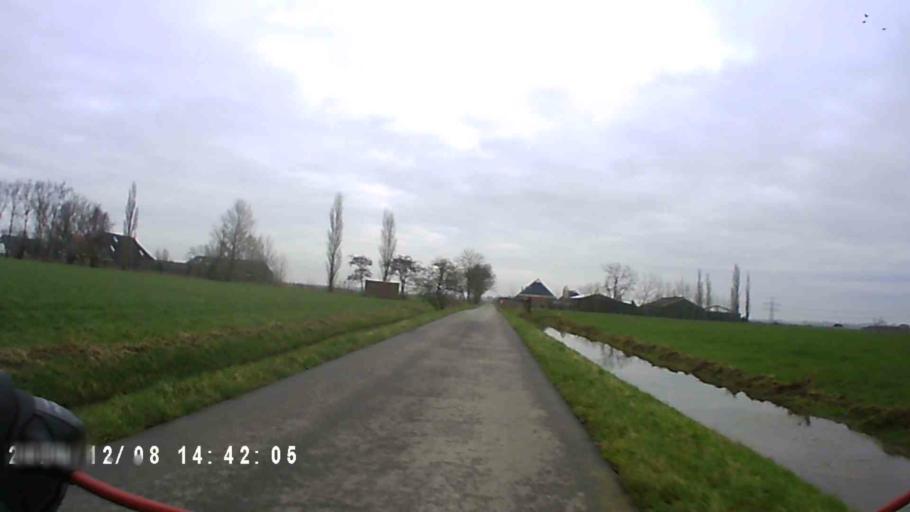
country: NL
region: Groningen
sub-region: Gemeente Winsum
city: Winsum
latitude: 53.3064
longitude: 6.5437
